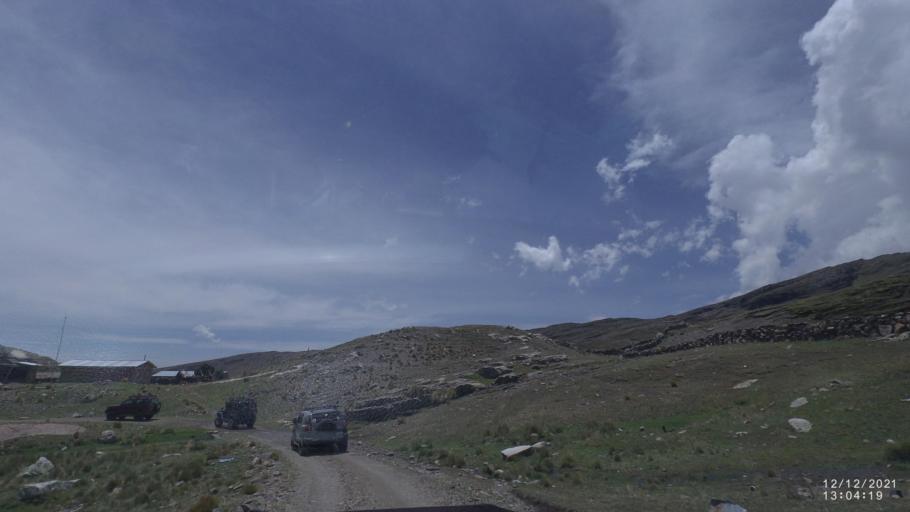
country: BO
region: Cochabamba
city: Cochabamba
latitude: -17.2676
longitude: -66.1684
